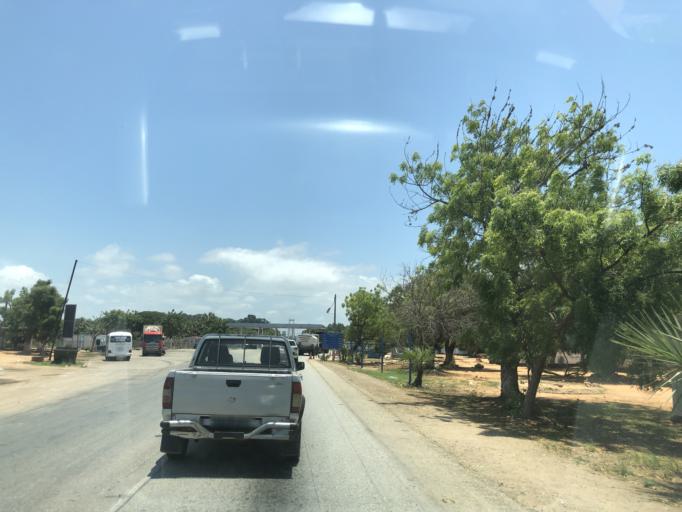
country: AO
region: Luanda
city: Luanda
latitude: -9.3178
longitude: 13.1551
